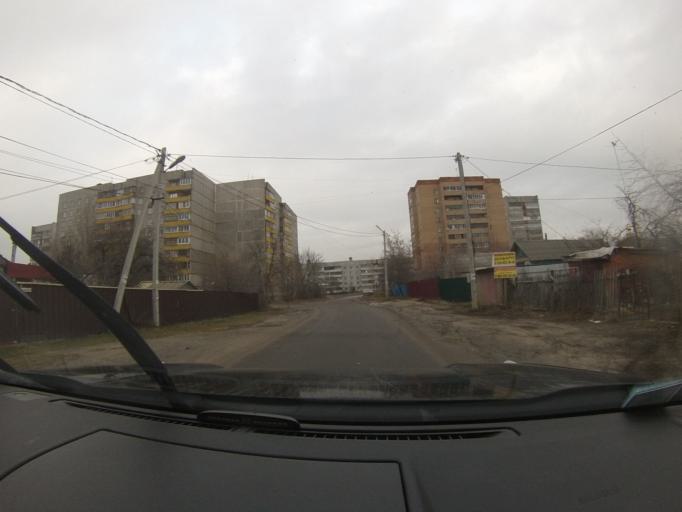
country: RU
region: Moskovskaya
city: Peski
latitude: 55.2695
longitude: 38.7538
